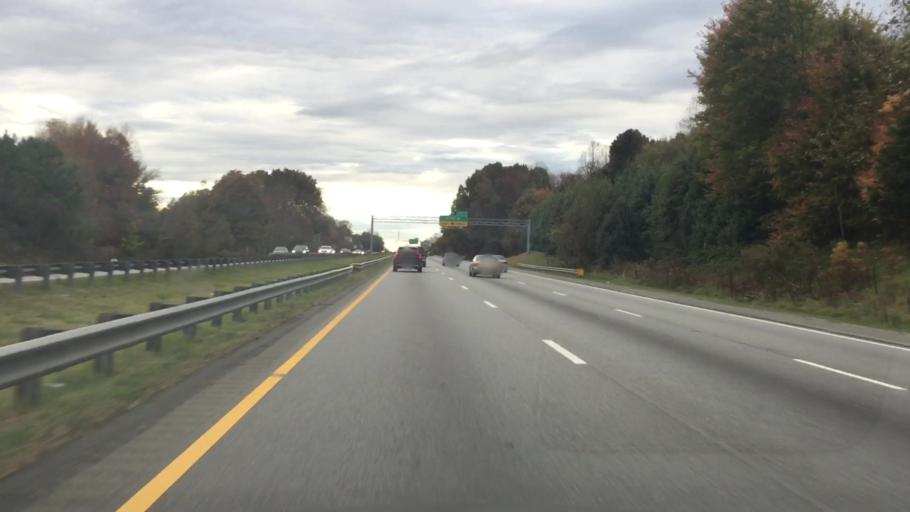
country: US
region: North Carolina
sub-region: Forsyth County
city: Winston-Salem
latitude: 36.0990
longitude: -80.2037
